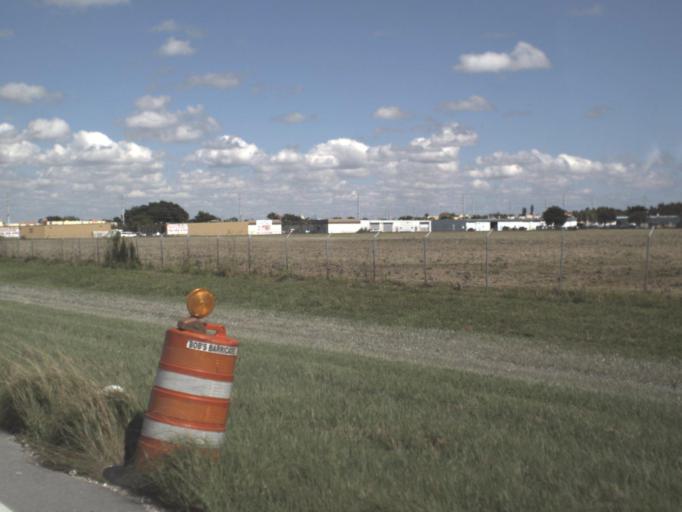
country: US
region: Florida
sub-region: Miami-Dade County
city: South Miami Heights
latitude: 25.5891
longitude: -80.3684
